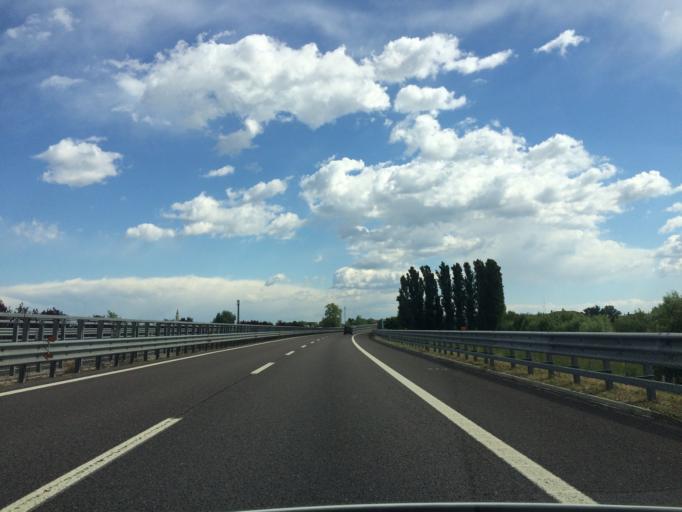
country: IT
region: Veneto
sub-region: Provincia di Vicenza
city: Villaggio Montegrappa
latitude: 45.5471
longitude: 11.6210
